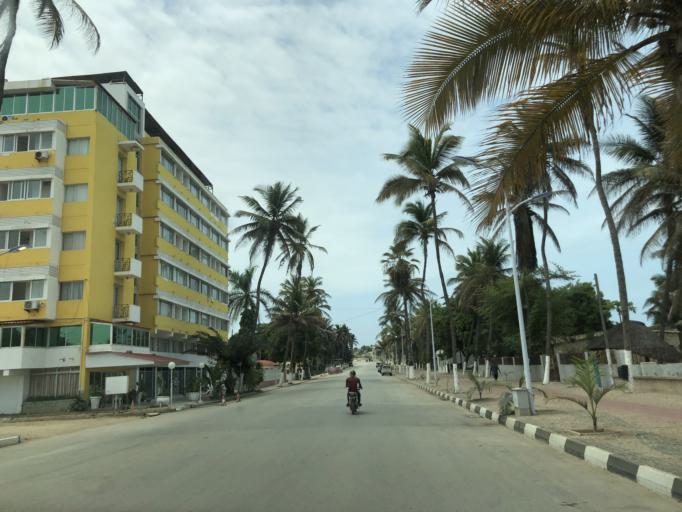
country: AO
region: Cuanza Sul
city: Sumbe
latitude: -11.1976
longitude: 13.8354
